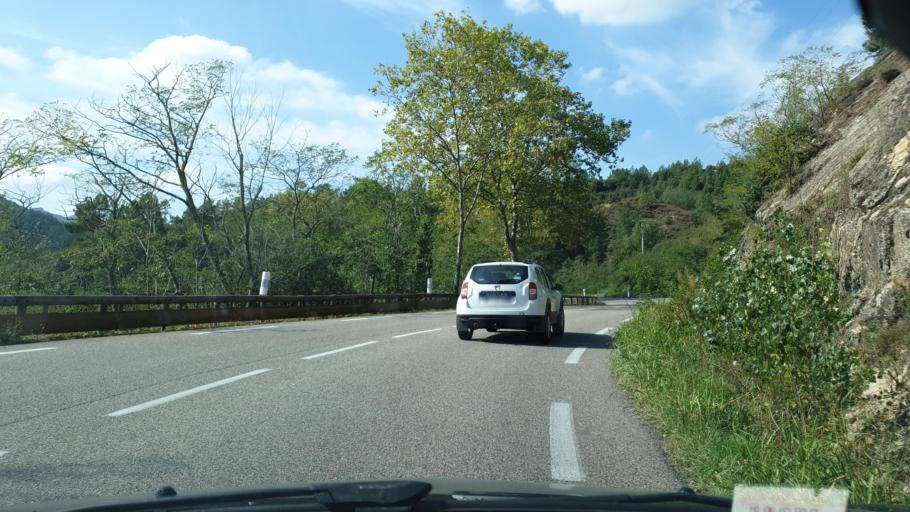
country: FR
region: Rhone-Alpes
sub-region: Departement de l'Ardeche
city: Saint-Laurent-du-Pape
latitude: 44.8192
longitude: 4.7142
